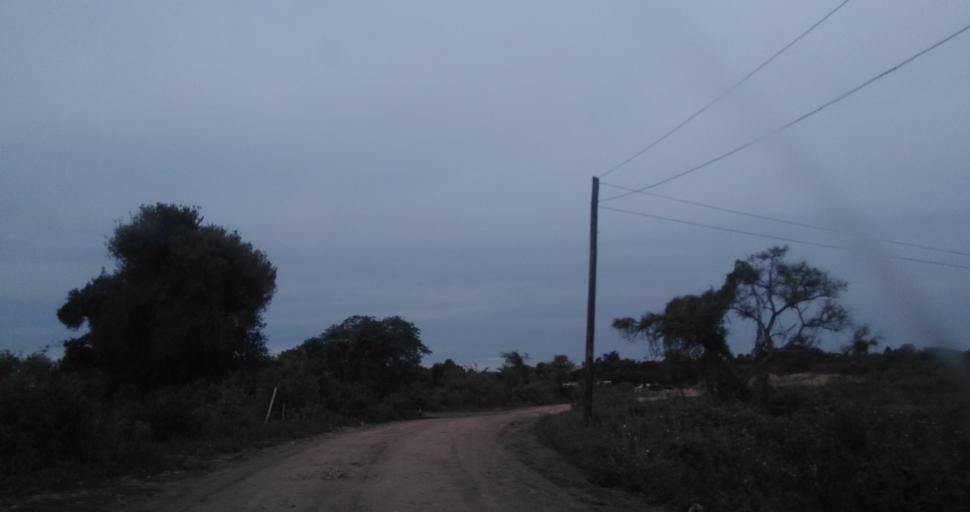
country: AR
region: Chaco
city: Fontana
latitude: -27.4047
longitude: -59.0224
